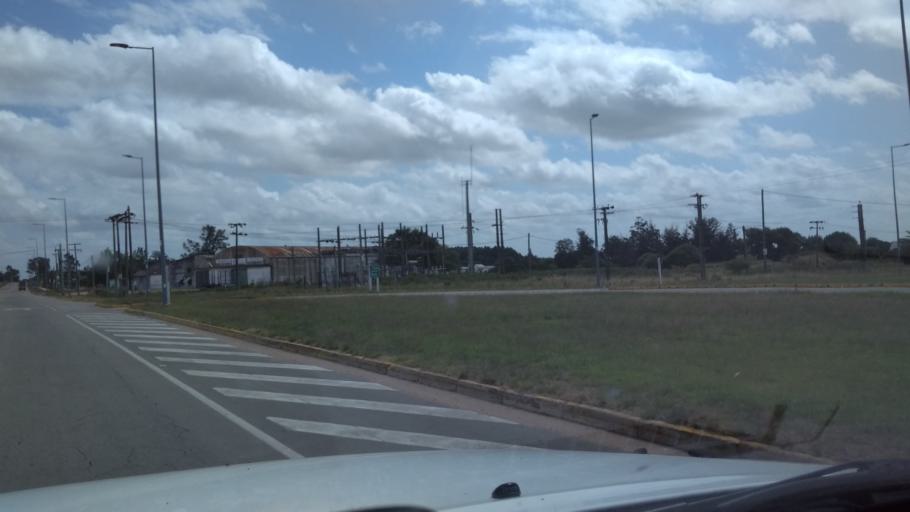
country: UY
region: Canelones
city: San Bautista
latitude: -34.4376
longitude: -55.9633
